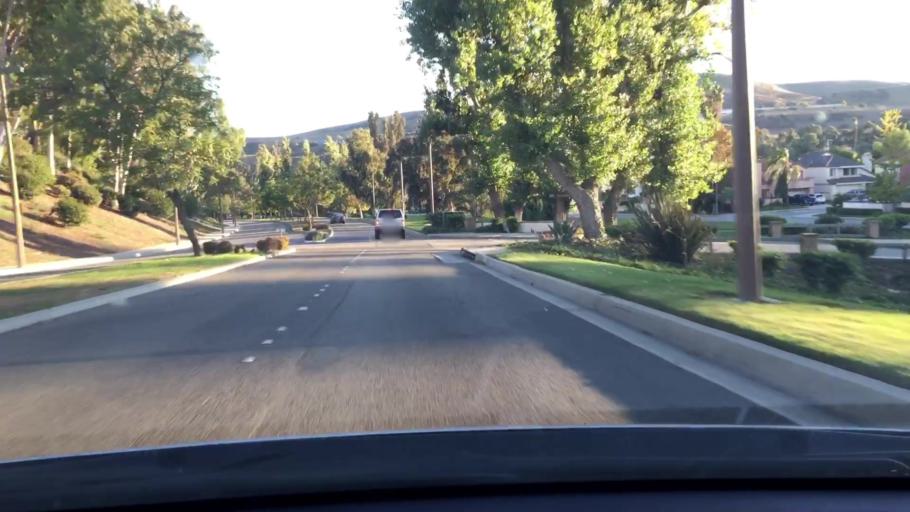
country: US
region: California
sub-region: Los Angeles County
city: Pomona
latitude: 34.0326
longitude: -117.7770
